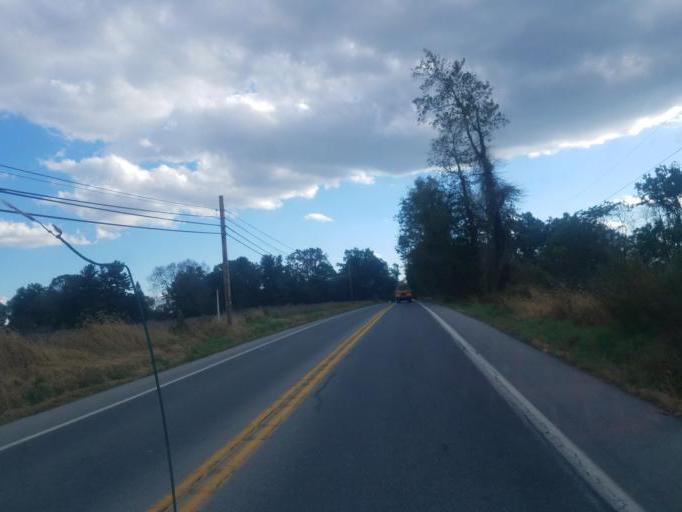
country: US
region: Pennsylvania
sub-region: Dauphin County
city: Middletown
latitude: 40.1612
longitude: -76.7175
